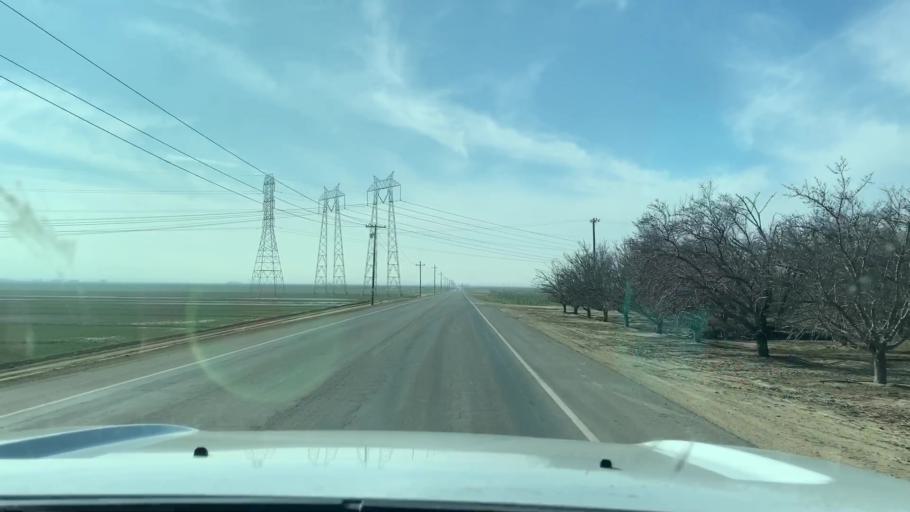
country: US
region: California
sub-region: Kern County
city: Buttonwillow
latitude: 35.4424
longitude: -119.4829
